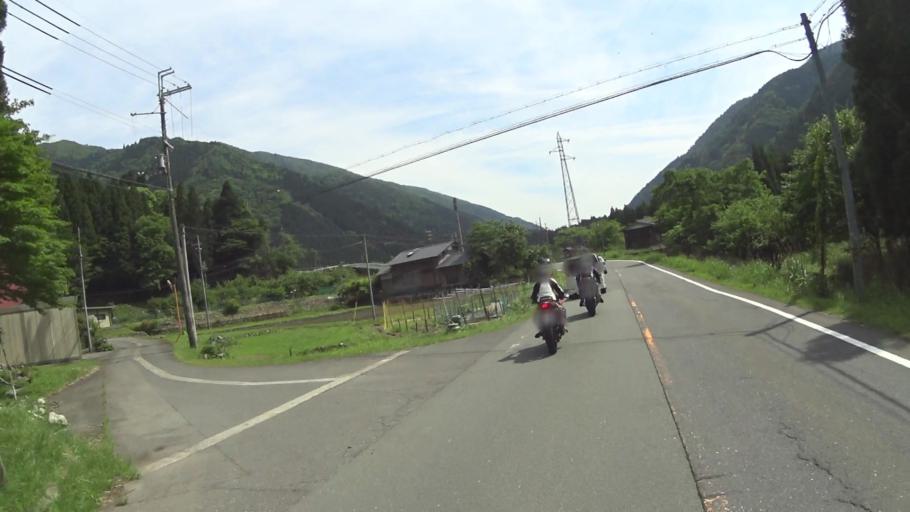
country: JP
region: Shiga Prefecture
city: Kitahama
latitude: 35.2911
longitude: 135.8836
